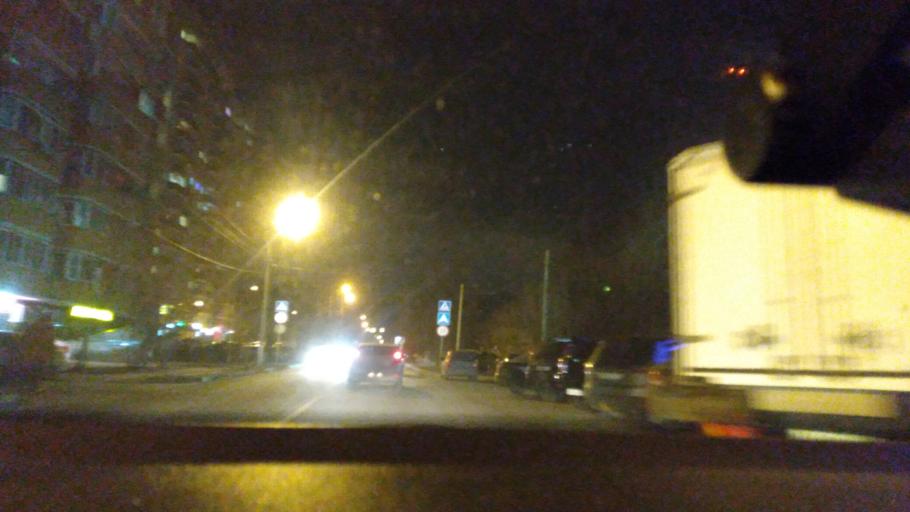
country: RU
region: Moskovskaya
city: Saltykovka
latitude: 55.7919
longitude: 37.9317
